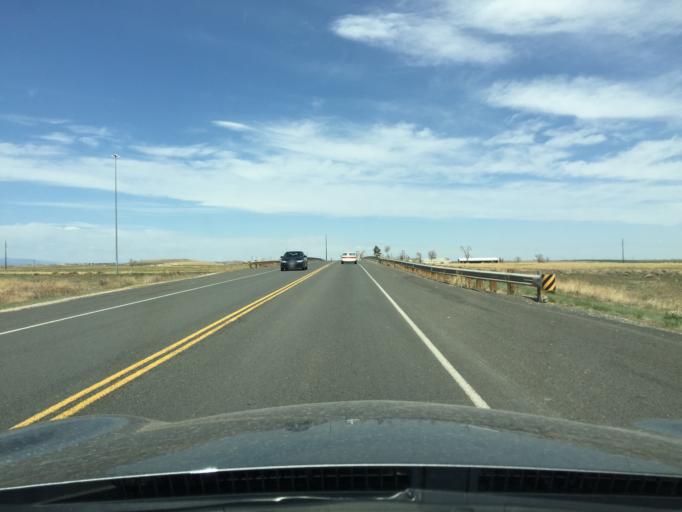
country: US
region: Colorado
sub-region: Boulder County
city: Erie
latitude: 39.9821
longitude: -104.9972
